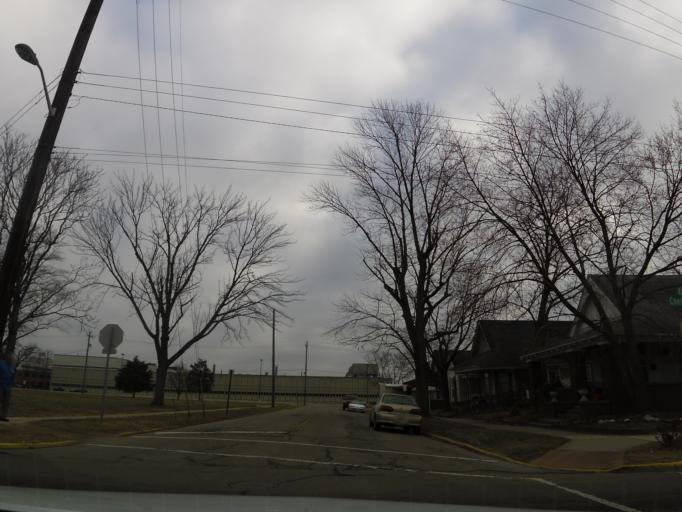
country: US
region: Indiana
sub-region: Bartholomew County
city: Columbus
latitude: 39.2027
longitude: -85.9145
